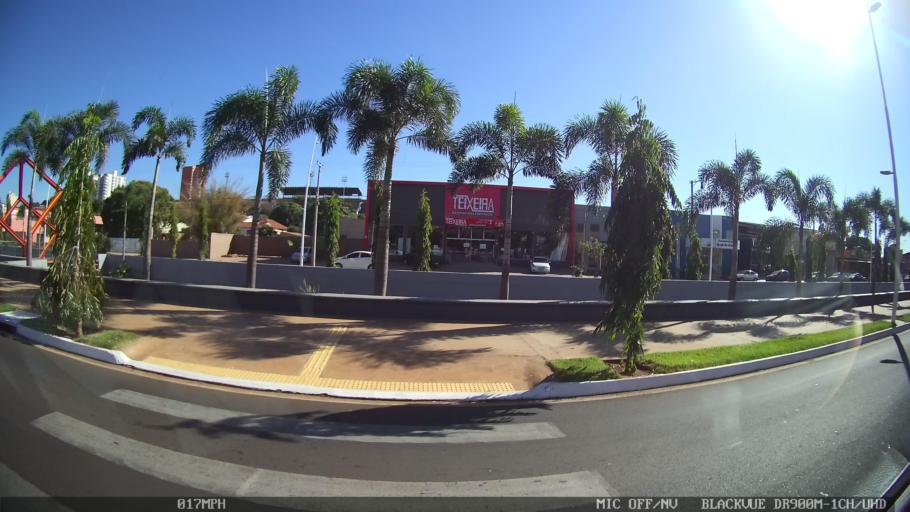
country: BR
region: Sao Paulo
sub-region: Olimpia
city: Olimpia
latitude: -20.7326
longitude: -48.9127
